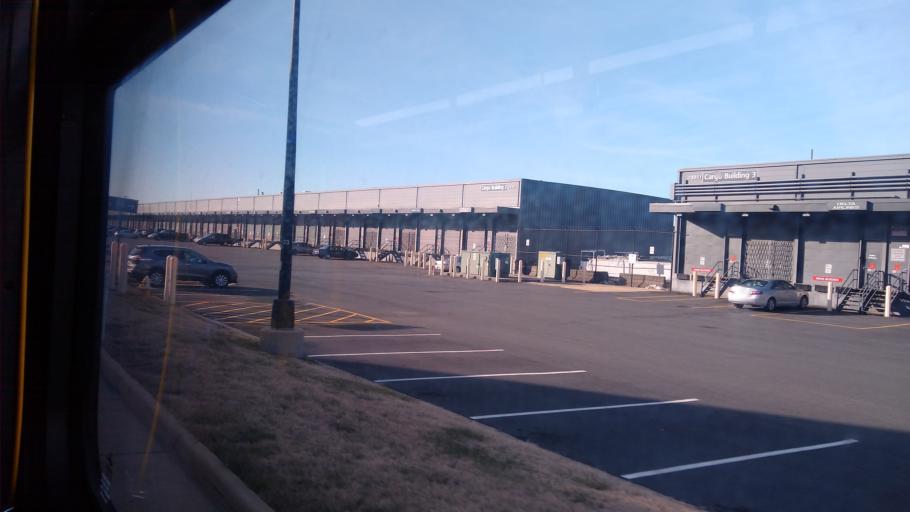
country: US
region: Virginia
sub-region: Fairfax County
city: Floris
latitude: 38.9559
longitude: -77.4530
